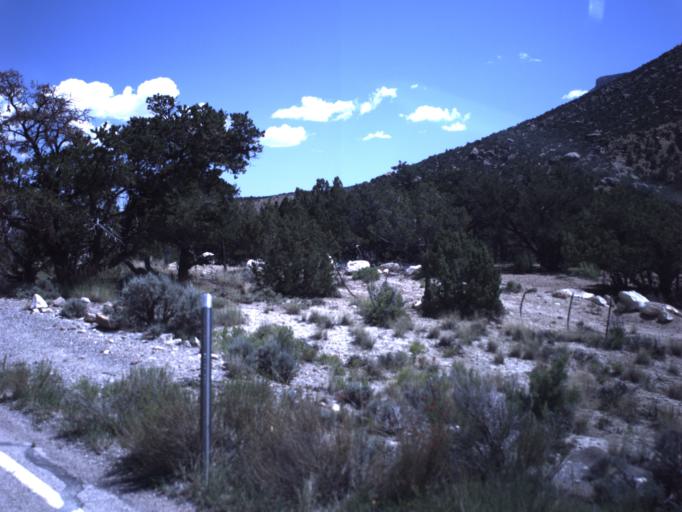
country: US
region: Utah
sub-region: Emery County
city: Orangeville
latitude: 39.2767
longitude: -111.1771
